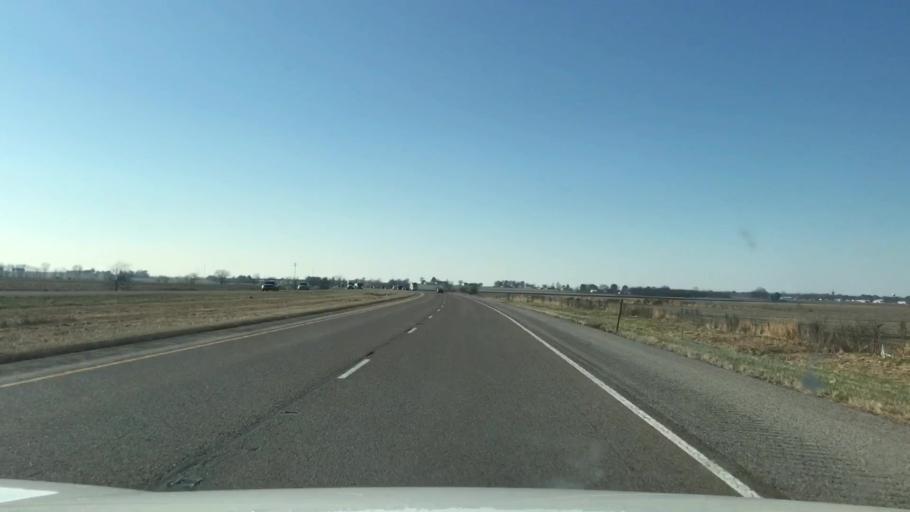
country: US
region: Illinois
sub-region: Clinton County
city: New Baden
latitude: 38.5156
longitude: -89.6627
